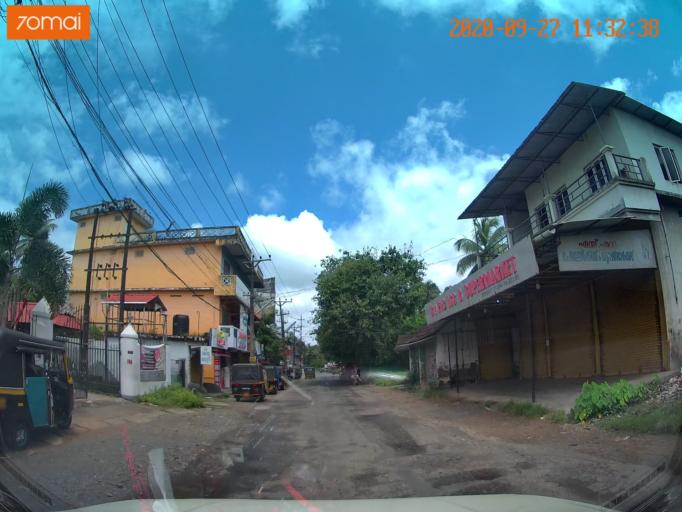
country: IN
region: Kerala
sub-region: Thrissur District
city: Thanniyam
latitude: 10.4278
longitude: 76.1303
